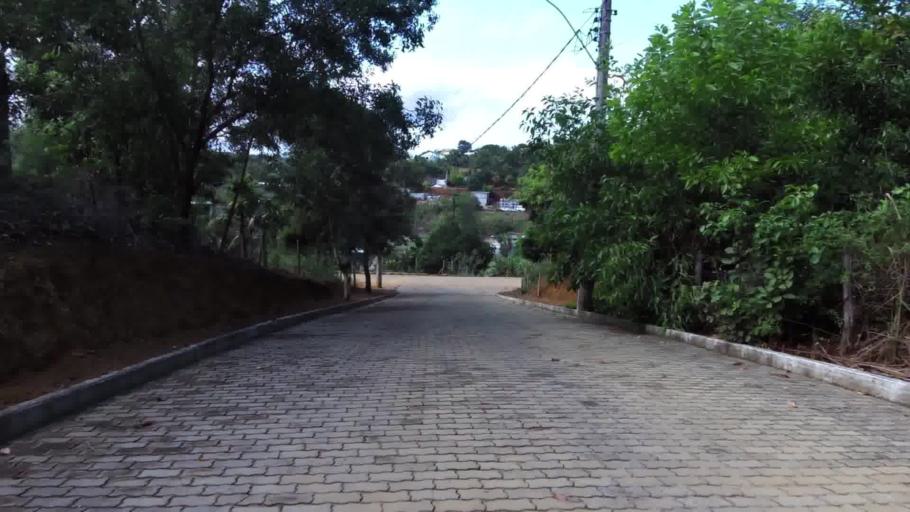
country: BR
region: Espirito Santo
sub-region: Piuma
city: Piuma
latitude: -20.8250
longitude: -40.6881
